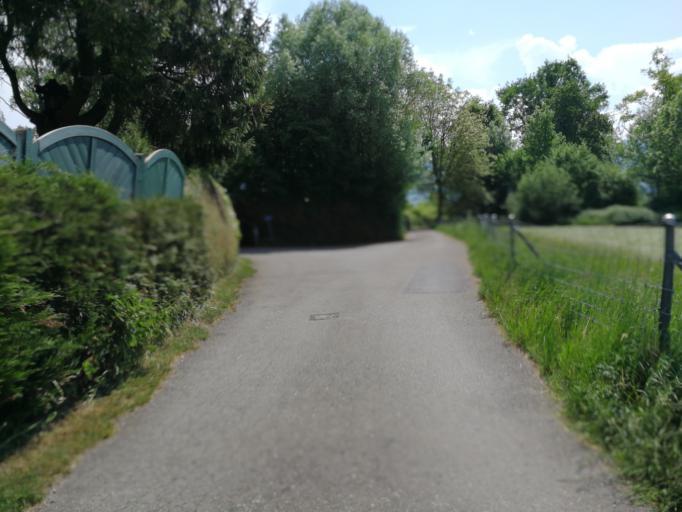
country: CH
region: Saint Gallen
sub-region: Wahlkreis See-Gaster
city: Jona
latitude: 47.2180
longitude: 8.8481
